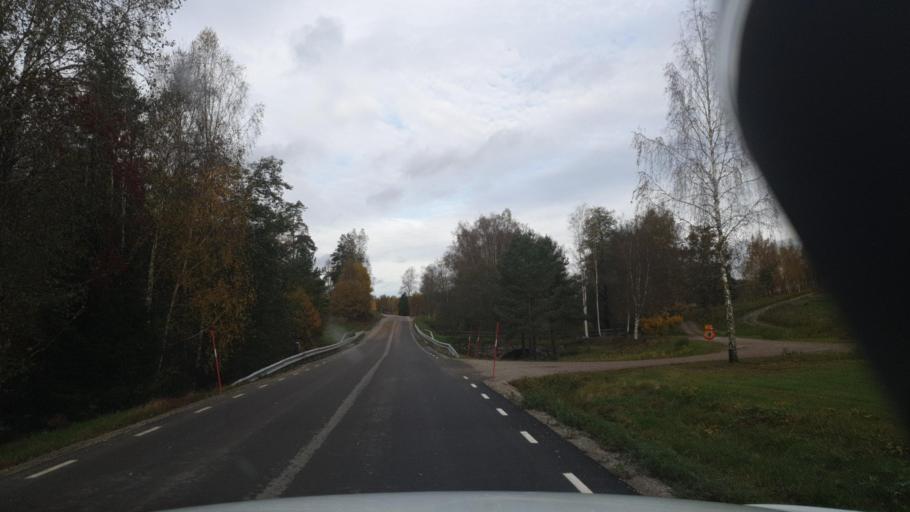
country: SE
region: Vaermland
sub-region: Sunne Kommun
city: Sunne
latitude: 59.6797
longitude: 12.8976
